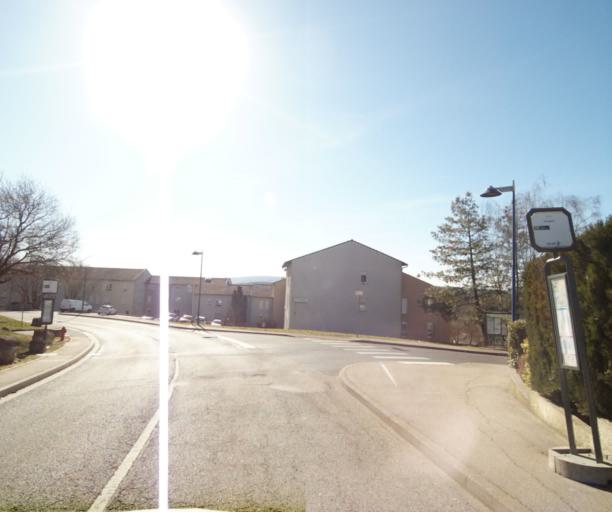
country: FR
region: Lorraine
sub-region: Departement de Meurthe-et-Moselle
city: Ludres
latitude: 48.6152
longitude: 6.1642
